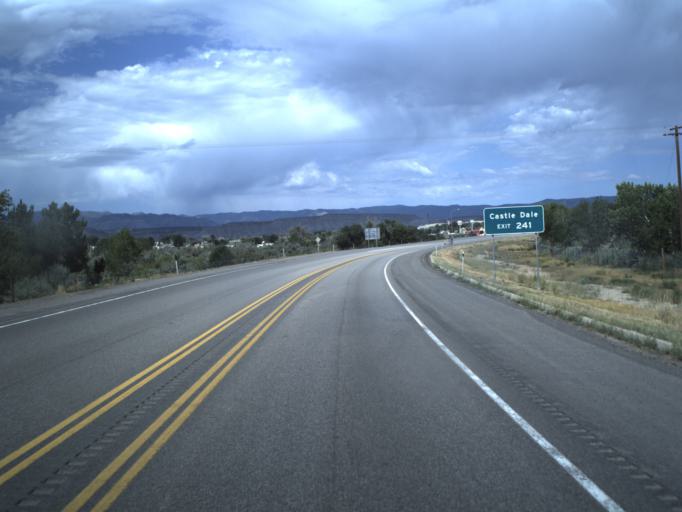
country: US
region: Utah
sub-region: Carbon County
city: Price
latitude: 39.5853
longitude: -110.8024
